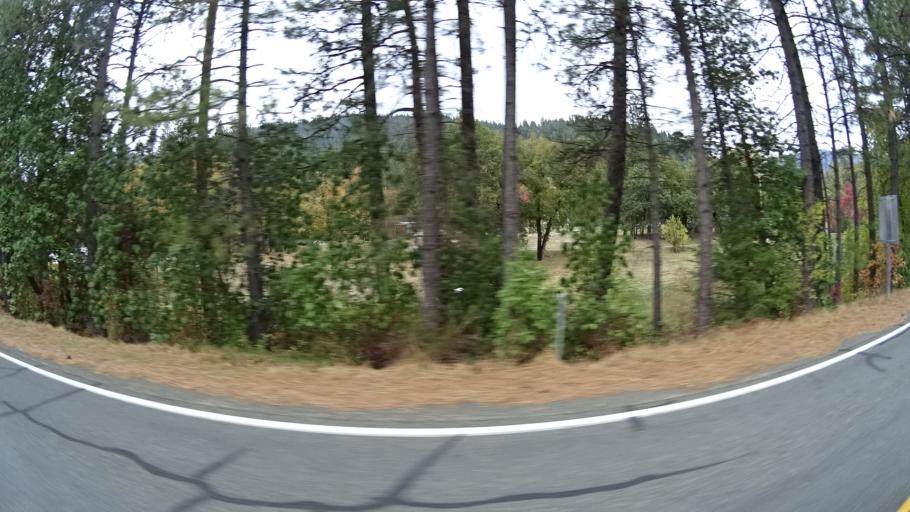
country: US
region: California
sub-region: Siskiyou County
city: Happy Camp
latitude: 41.7894
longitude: -123.3819
